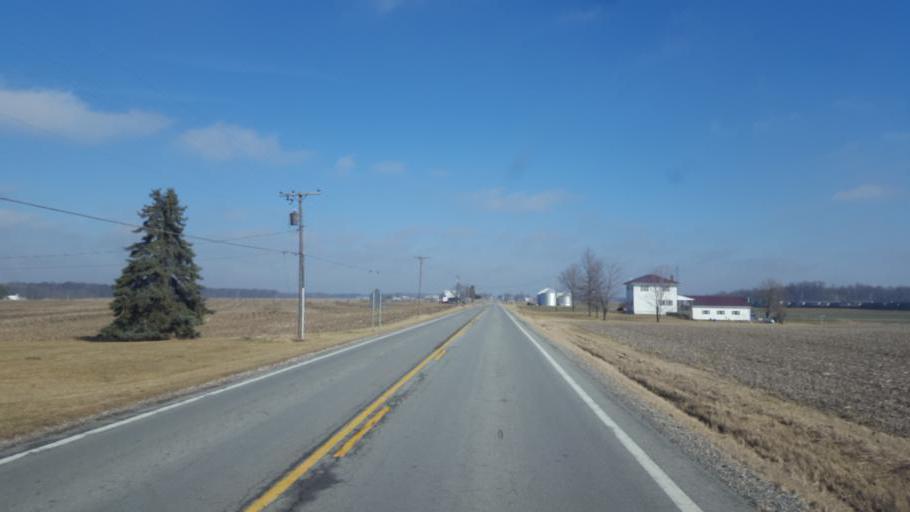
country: US
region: Ohio
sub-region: Crawford County
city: Bucyrus
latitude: 40.9808
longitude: -82.9291
